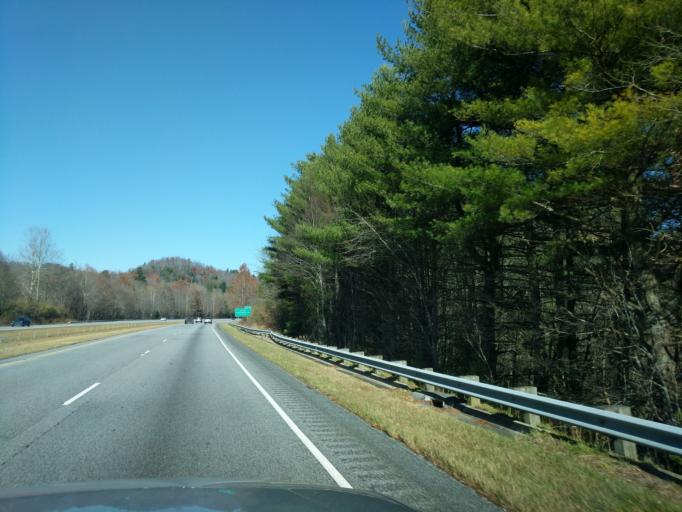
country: US
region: North Carolina
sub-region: Henderson County
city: Flat Rock
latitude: 35.2009
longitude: -82.4512
